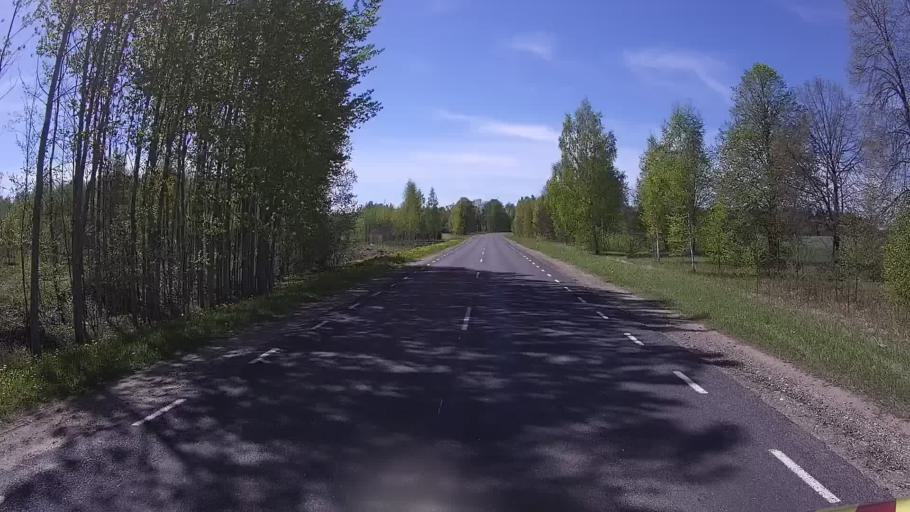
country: EE
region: Polvamaa
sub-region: Raepina vald
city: Rapina
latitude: 58.0143
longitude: 27.3607
